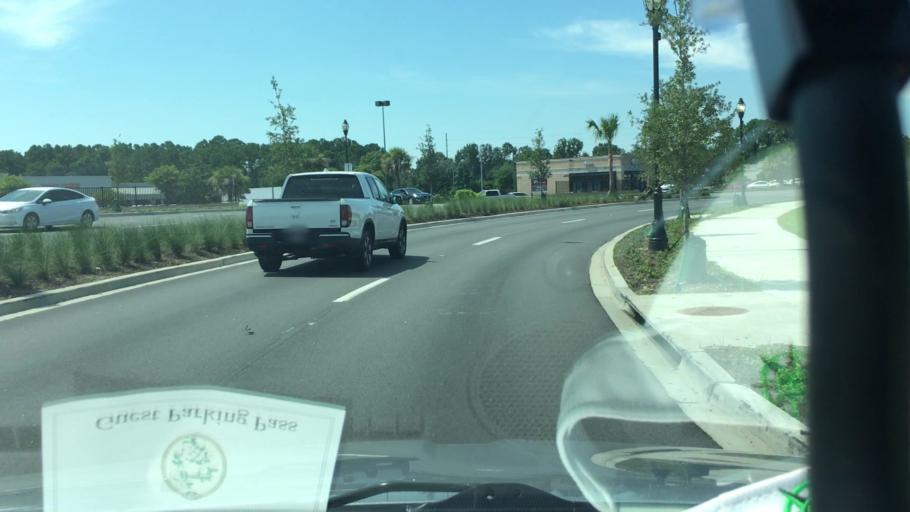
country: US
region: South Carolina
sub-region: Beaufort County
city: Burton
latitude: 32.4400
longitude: -80.7053
